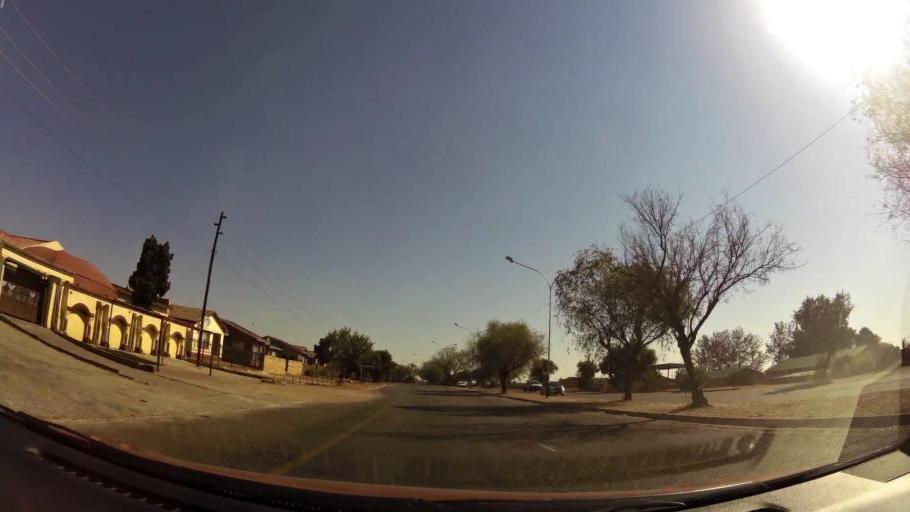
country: ZA
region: Gauteng
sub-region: City of Tshwane Metropolitan Municipality
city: Mabopane
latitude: -25.5248
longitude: 28.1053
